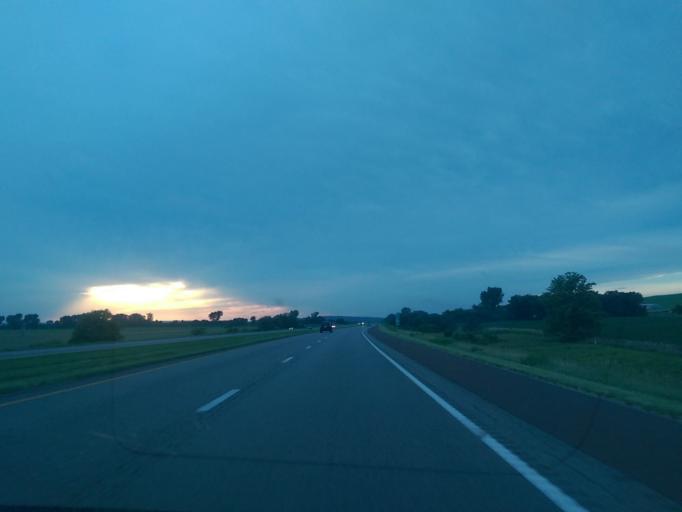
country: US
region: Missouri
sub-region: Holt County
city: Mound City
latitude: 40.1706
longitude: -95.2984
